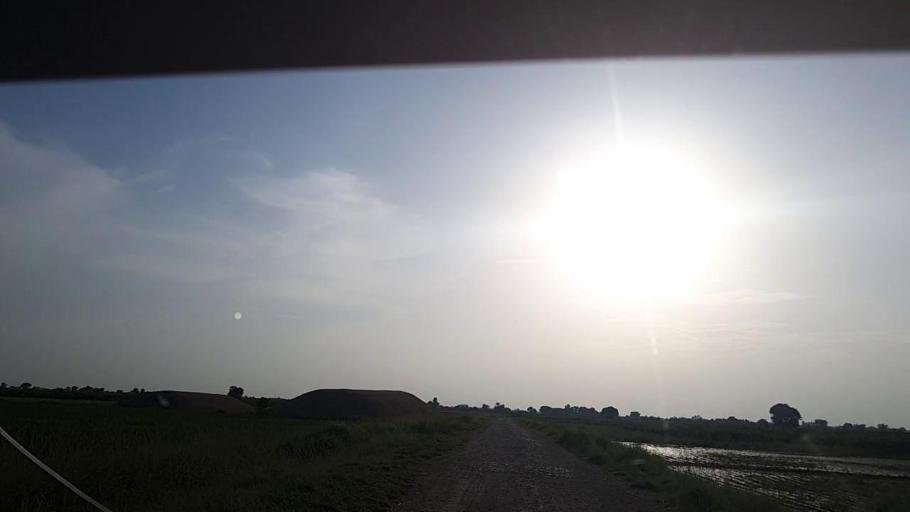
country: PK
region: Sindh
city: Khanpur
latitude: 27.8088
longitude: 69.3222
